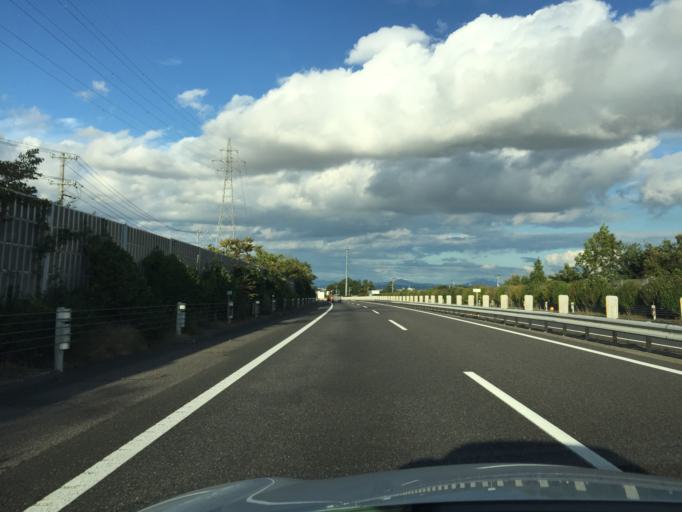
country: JP
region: Fukushima
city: Koriyama
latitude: 37.4112
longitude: 140.3247
